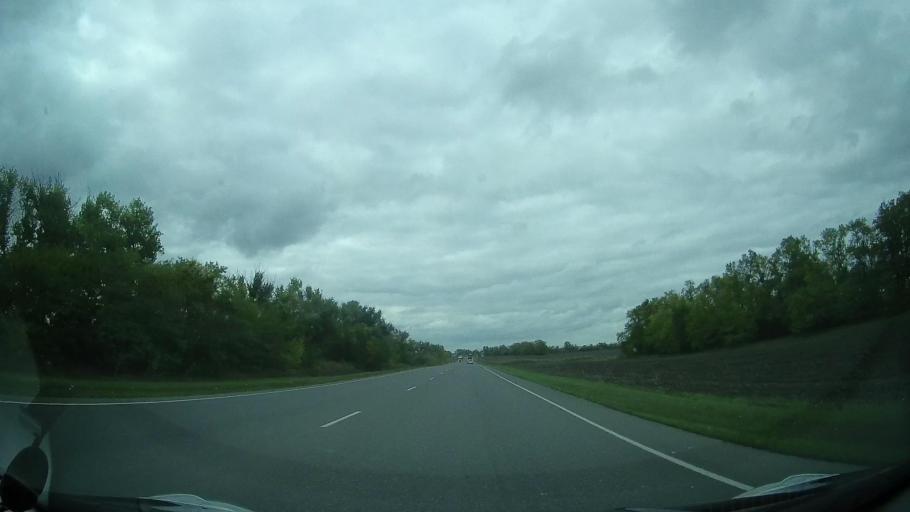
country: RU
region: Rostov
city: Mechetinskaya
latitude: 46.7470
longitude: 40.4648
